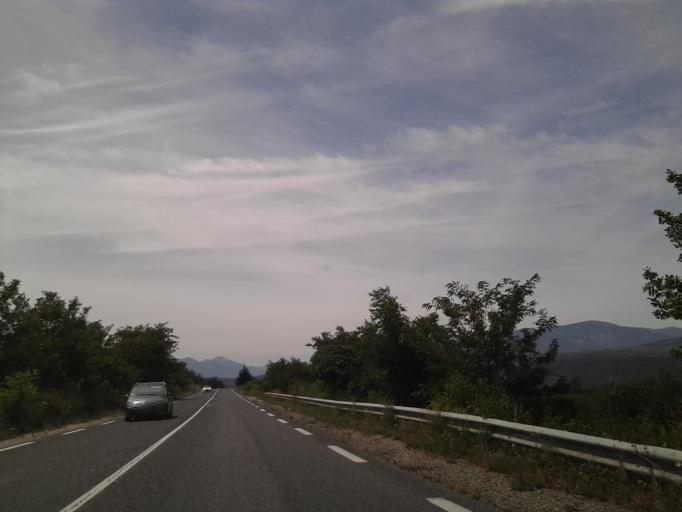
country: FR
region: Languedoc-Roussillon
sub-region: Departement des Pyrenees-Orientales
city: Prades
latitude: 42.6362
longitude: 2.4687
